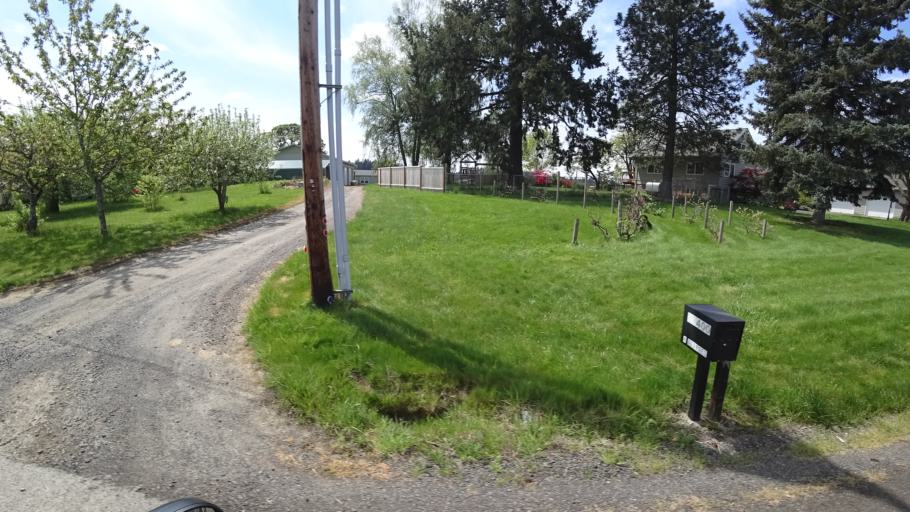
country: US
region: Oregon
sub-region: Washington County
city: North Plains
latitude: 45.5717
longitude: -122.9596
